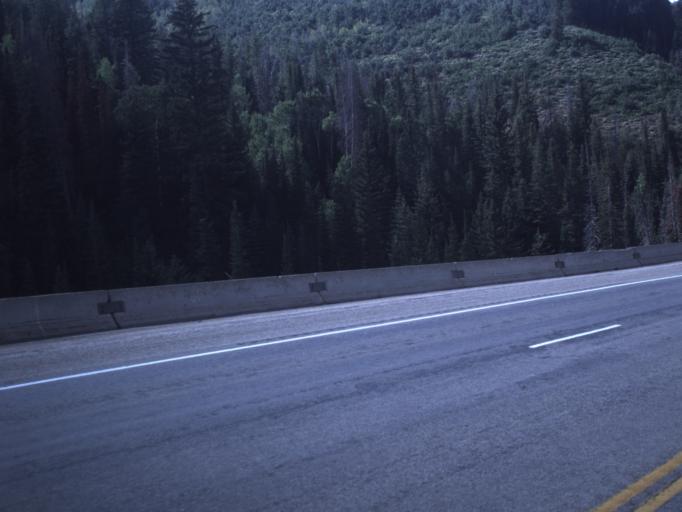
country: US
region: Utah
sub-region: Wasatch County
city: Heber
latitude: 40.3244
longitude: -111.2617
